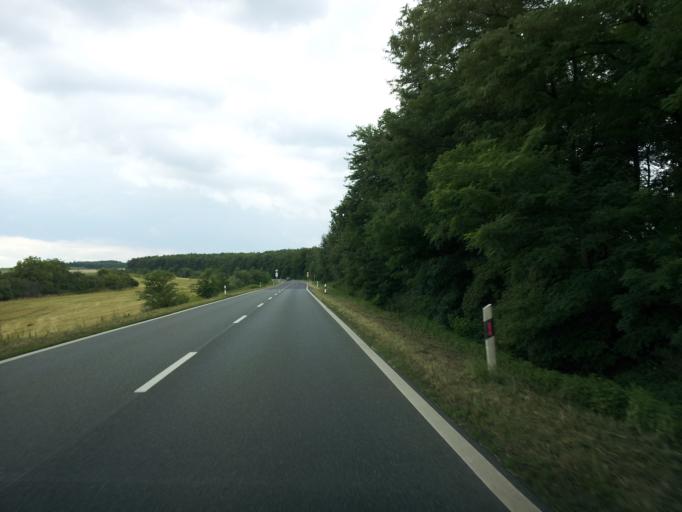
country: HU
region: Zala
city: Turje
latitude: 47.0998
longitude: 17.0008
